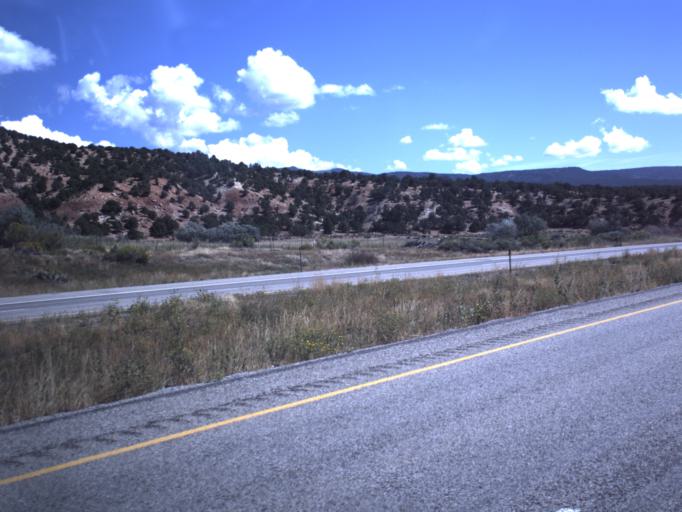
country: US
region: Utah
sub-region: Sevier County
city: Salina
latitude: 38.9199
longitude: -111.7539
